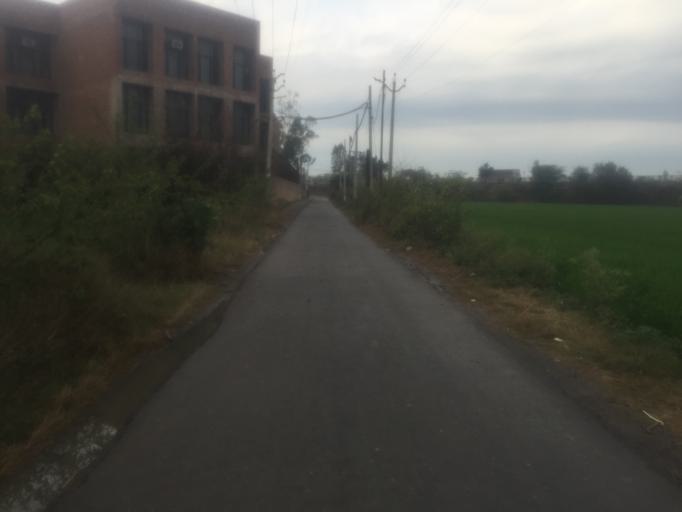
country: IN
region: Punjab
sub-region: Kapurthala
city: Phagwara
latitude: 31.2581
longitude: 75.7092
